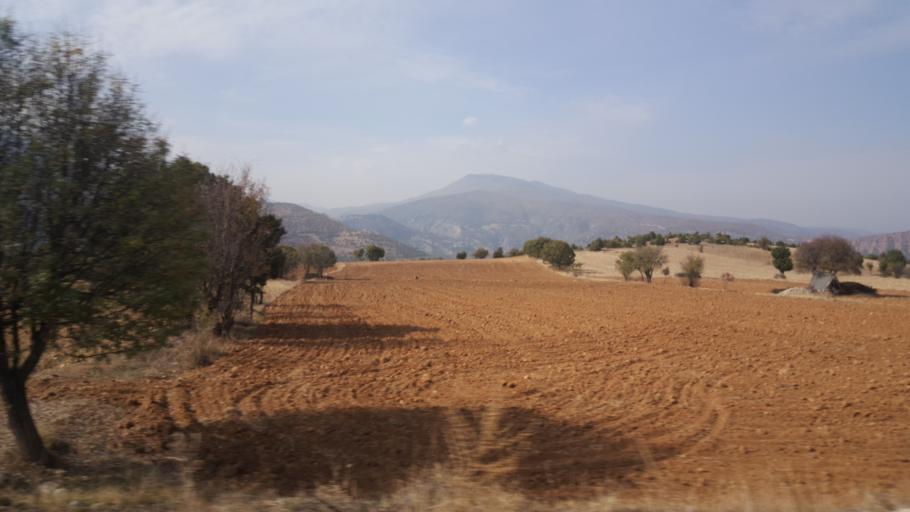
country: TR
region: Eskisehir
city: Mihaliccik
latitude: 39.9856
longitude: 31.3800
